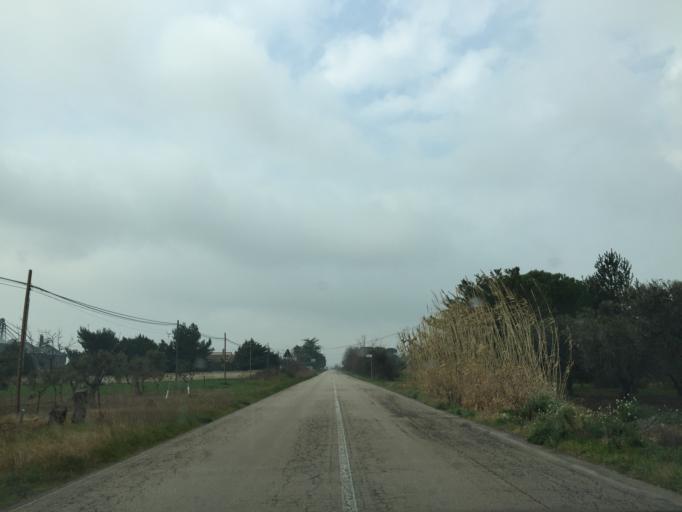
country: IT
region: Apulia
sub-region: Provincia di Foggia
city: Troia
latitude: 41.3823
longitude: 15.3775
